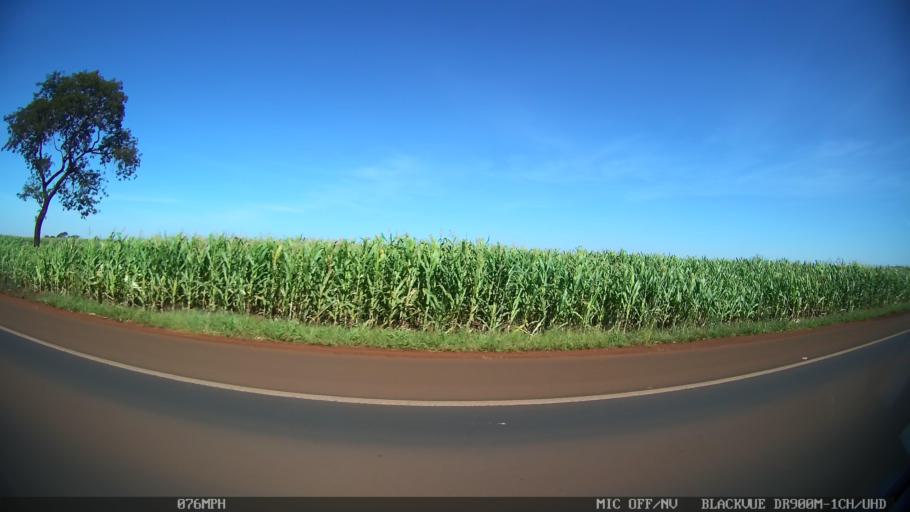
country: BR
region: Sao Paulo
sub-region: Guaira
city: Guaira
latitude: -20.4445
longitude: -48.3708
